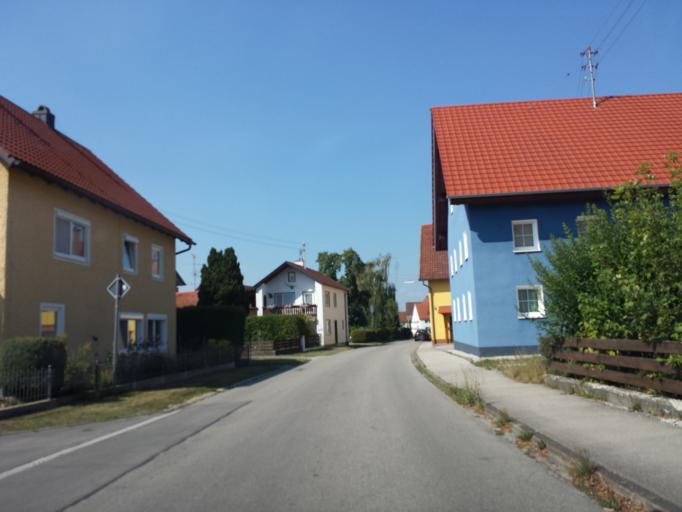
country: DE
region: Bavaria
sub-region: Swabia
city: Tussenhausen
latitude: 48.0670
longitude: 10.5816
